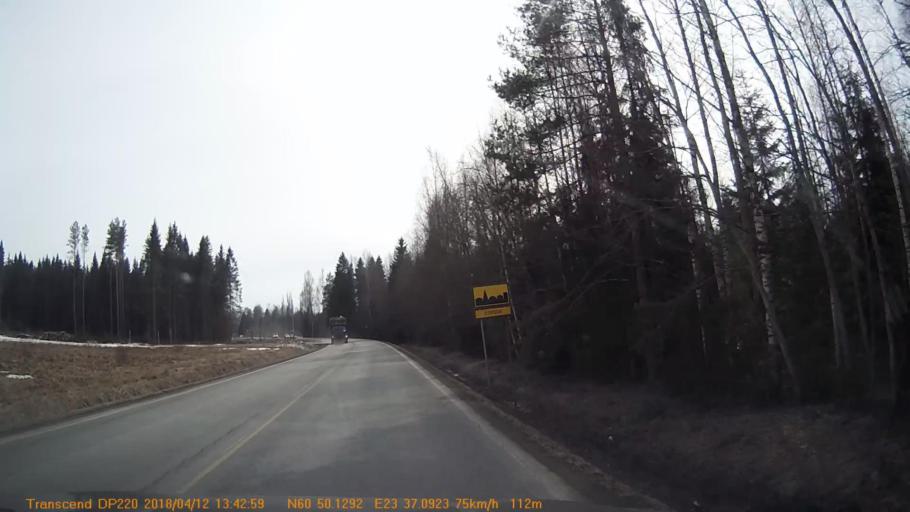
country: FI
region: Haeme
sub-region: Forssa
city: Forssa
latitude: 60.8349
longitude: 23.6182
